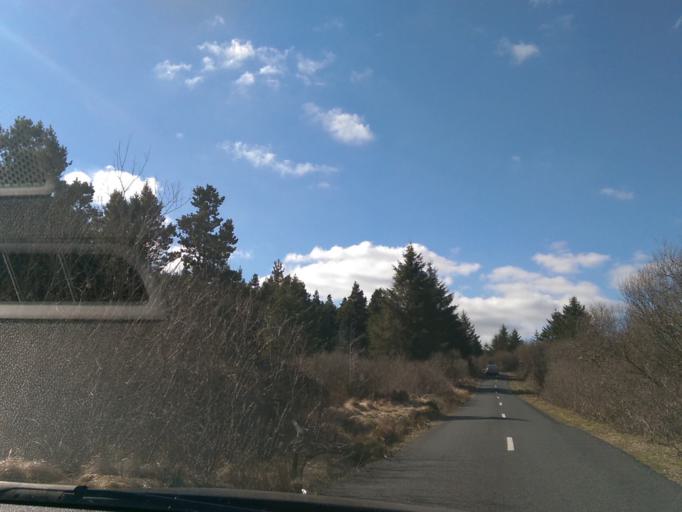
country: IE
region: Leinster
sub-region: Laois
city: Mountrath
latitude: 53.0738
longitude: -7.5845
